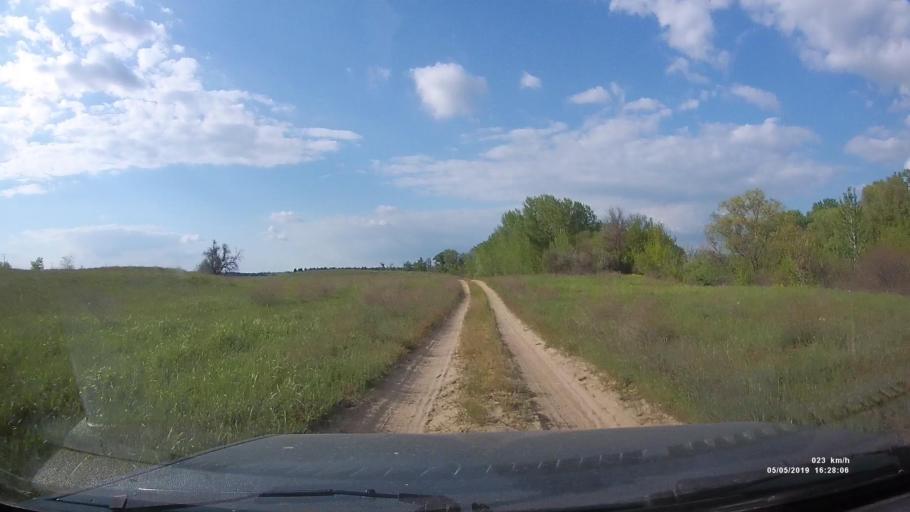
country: RU
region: Rostov
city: Ust'-Donetskiy
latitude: 47.7665
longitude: 41.0163
